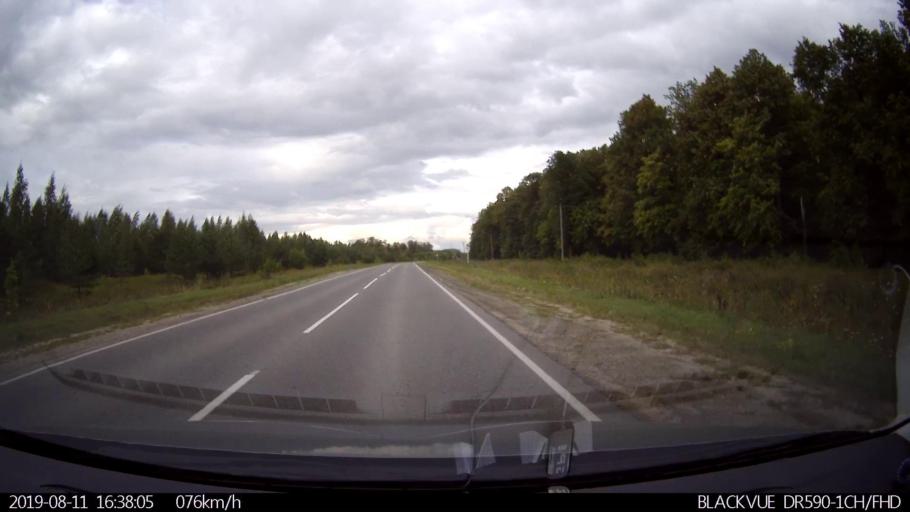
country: RU
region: Ulyanovsk
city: Mayna
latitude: 54.1323
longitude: 47.6205
